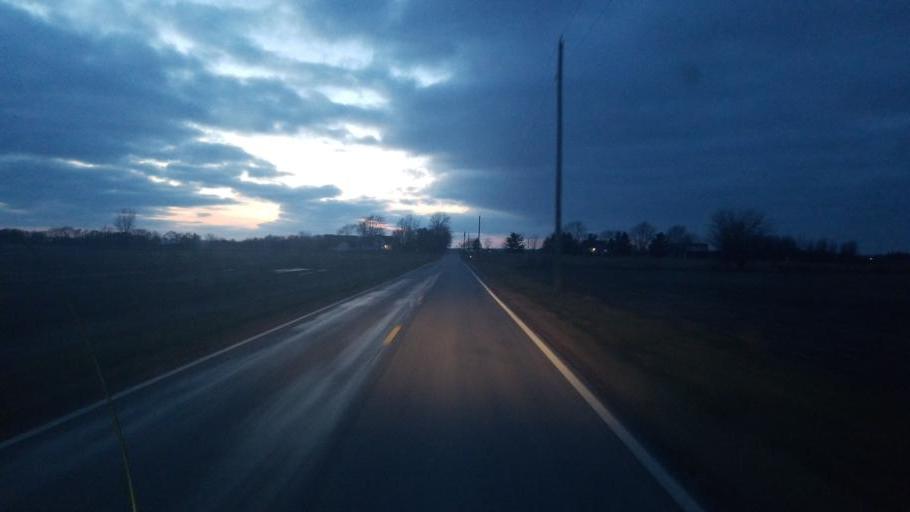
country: US
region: Ohio
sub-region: Marion County
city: Prospect
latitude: 40.4313
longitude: -83.1490
